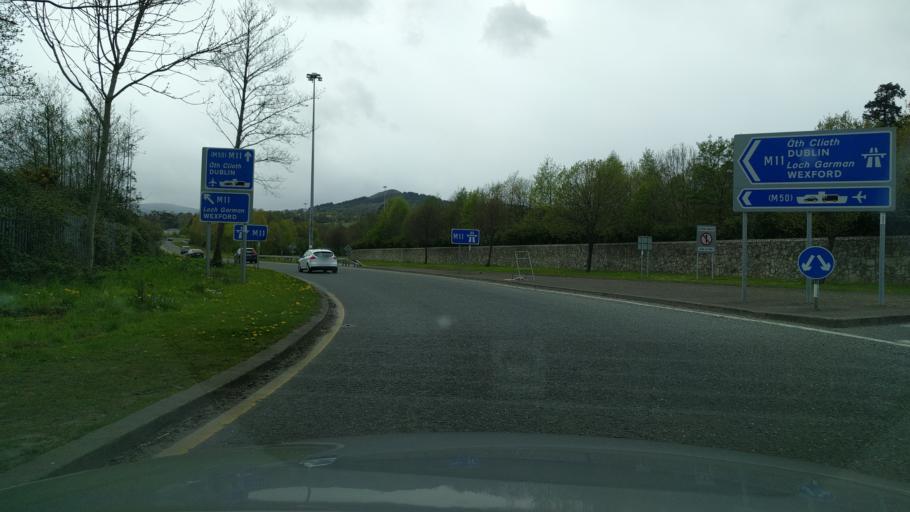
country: IE
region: Leinster
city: Little Bray
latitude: 53.2133
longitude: -6.1193
